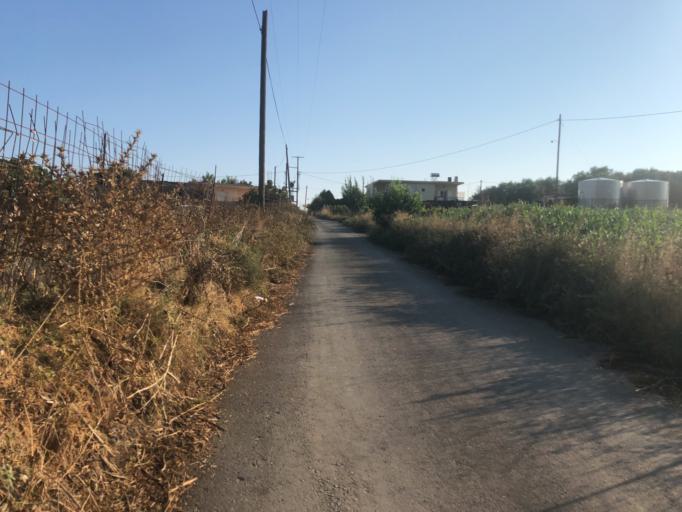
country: GR
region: Crete
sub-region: Nomos Chanias
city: Georgioupolis
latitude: 35.3485
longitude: 24.2873
